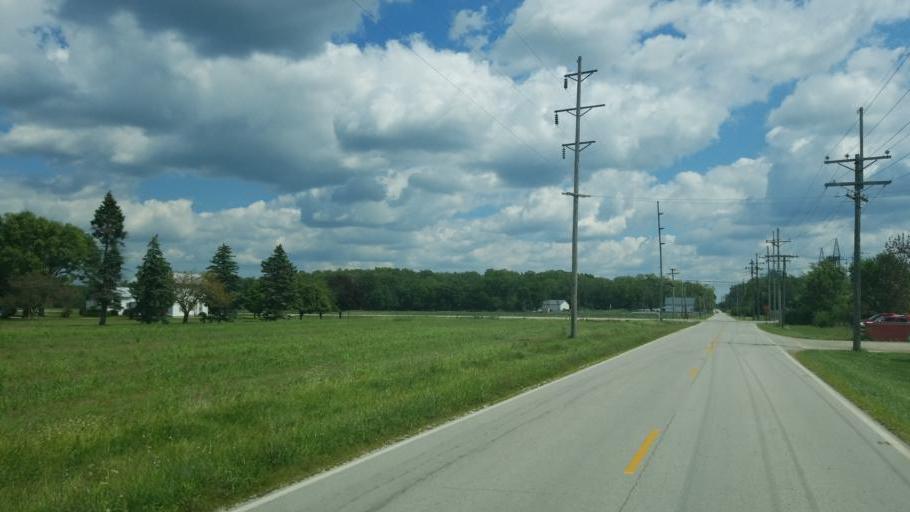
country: US
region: Ohio
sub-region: Sandusky County
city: Gibsonburg
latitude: 41.3990
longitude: -83.3211
